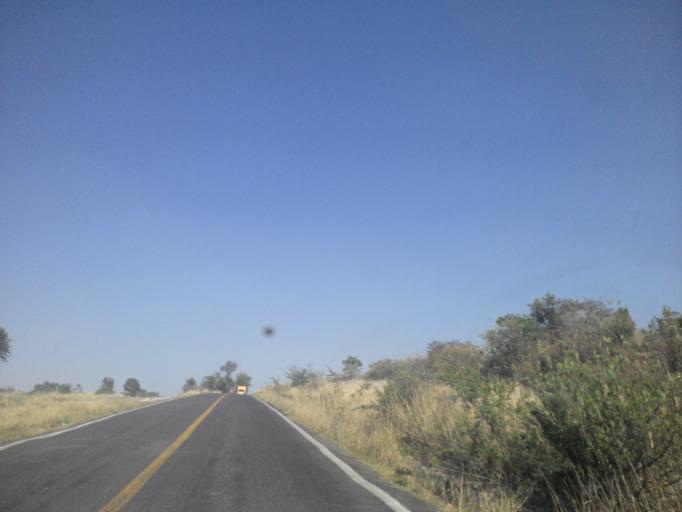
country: MX
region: Jalisco
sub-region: Arandas
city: Santiaguito (Santiaguito de Velazquez)
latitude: 20.7802
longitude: -102.2834
